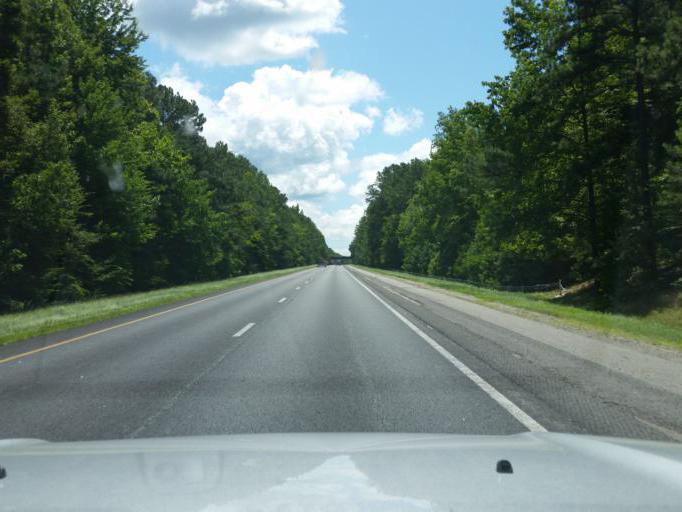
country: US
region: Virginia
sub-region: New Kent County
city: New Kent
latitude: 37.4631
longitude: -76.8885
